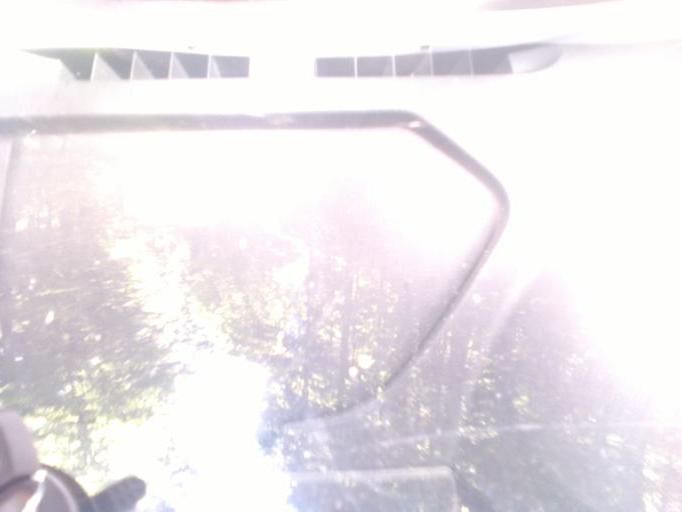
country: FR
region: Lorraine
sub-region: Departement des Vosges
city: Xonrupt-Longemer
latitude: 48.0229
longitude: 6.9658
